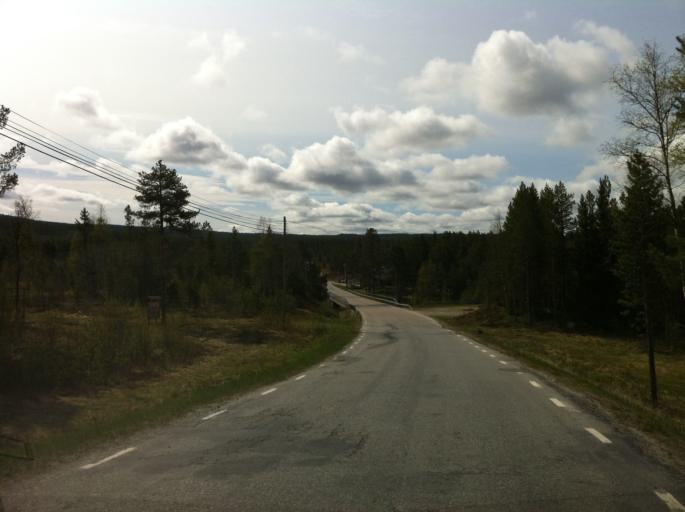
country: NO
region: Hedmark
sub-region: Engerdal
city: Engerdal
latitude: 62.4417
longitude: 12.6846
